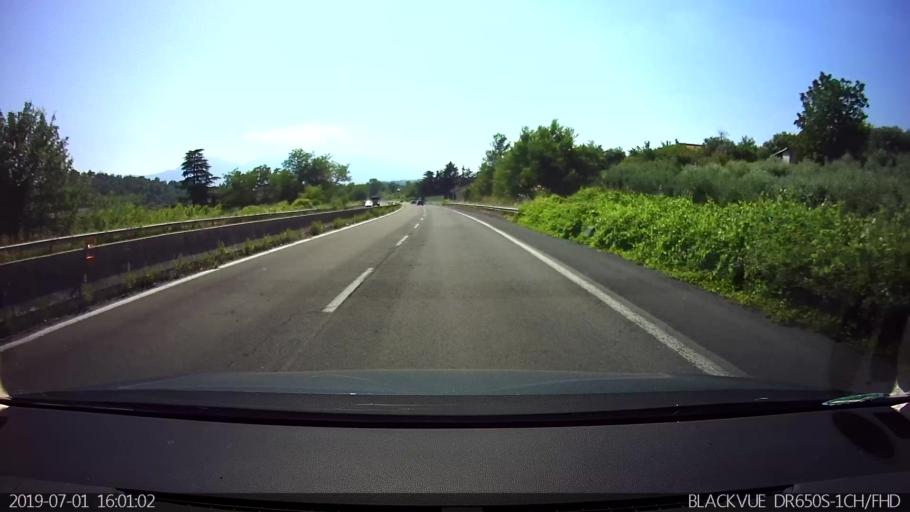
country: IT
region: Latium
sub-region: Provincia di Frosinone
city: Castelmassimo
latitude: 41.6645
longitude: 13.3827
